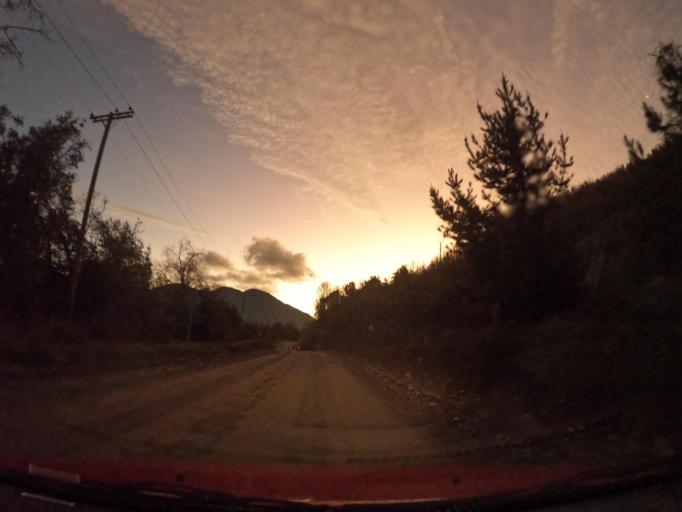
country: CL
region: Maule
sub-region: Provincia de Linares
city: Colbun
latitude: -35.8584
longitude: -71.2355
